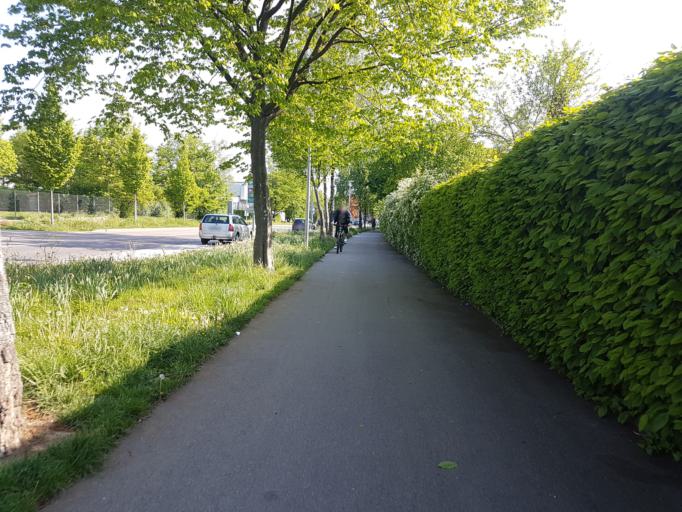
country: DE
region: Baden-Wuerttemberg
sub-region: Regierungsbezirk Stuttgart
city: Kornwestheim
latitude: 48.8529
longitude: 9.1845
